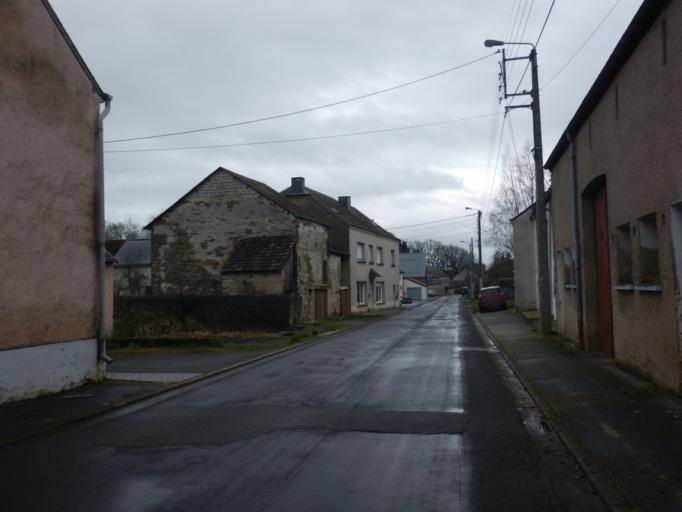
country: BE
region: Wallonia
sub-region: Province du Luxembourg
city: Attert
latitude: 49.7723
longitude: 5.7887
